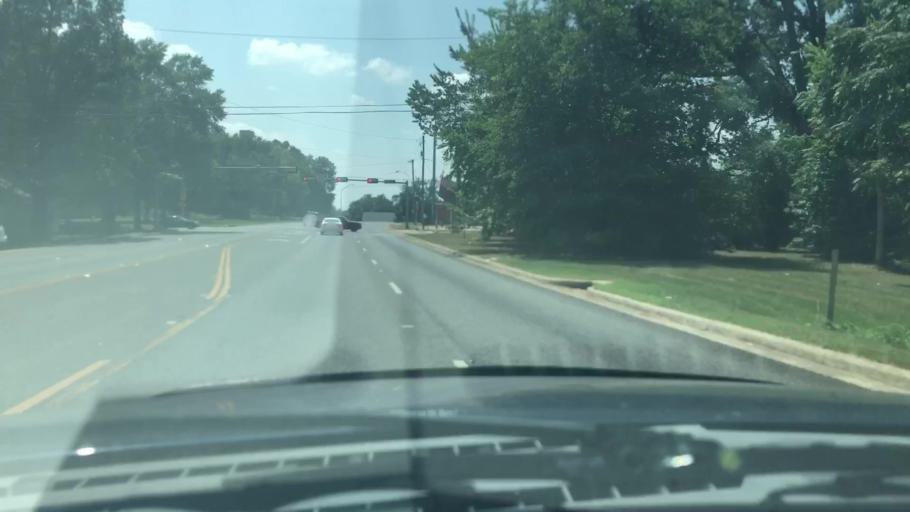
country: US
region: Texas
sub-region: Bowie County
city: Texarkana
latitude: 33.4300
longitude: -94.0616
